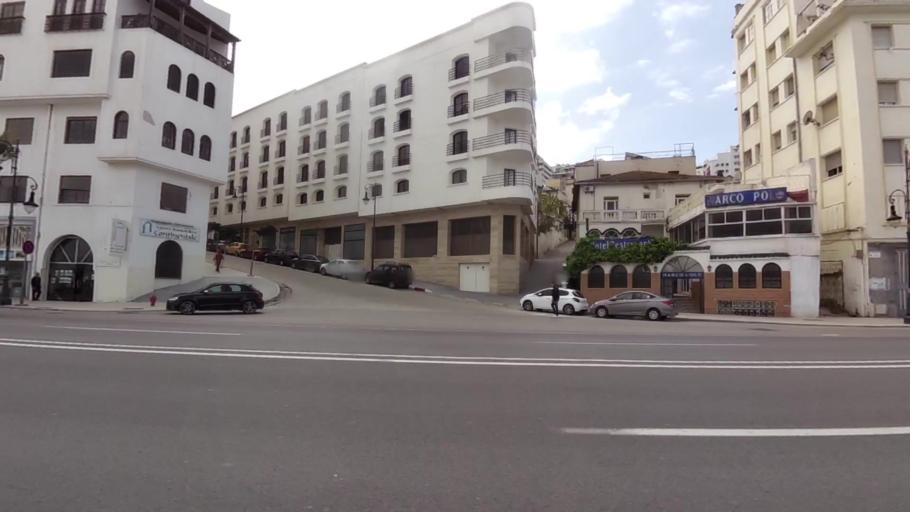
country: MA
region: Tanger-Tetouan
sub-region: Tanger-Assilah
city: Tangier
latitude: 35.7813
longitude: -5.8058
